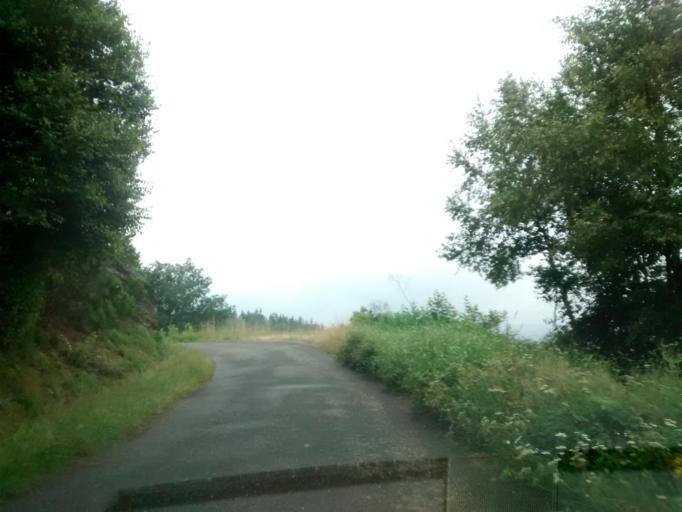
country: ES
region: Galicia
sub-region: Provincia de Ourense
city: Castro Caldelas
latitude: 42.4068
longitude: -7.3981
